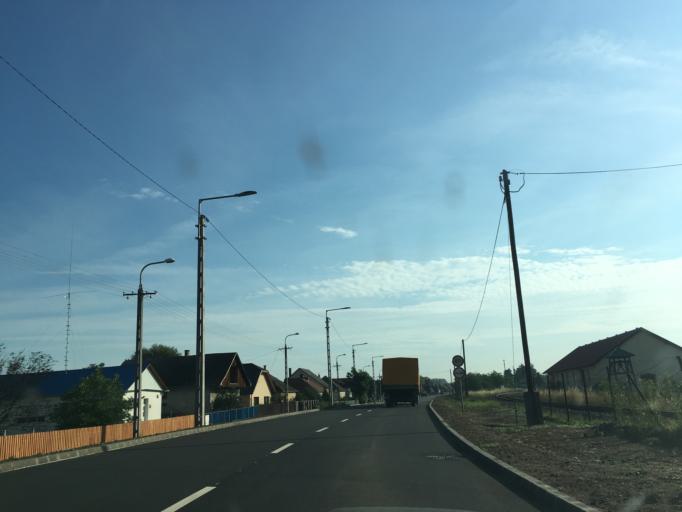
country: HU
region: Hajdu-Bihar
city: Nyiradony
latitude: 47.6601
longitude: 21.8390
